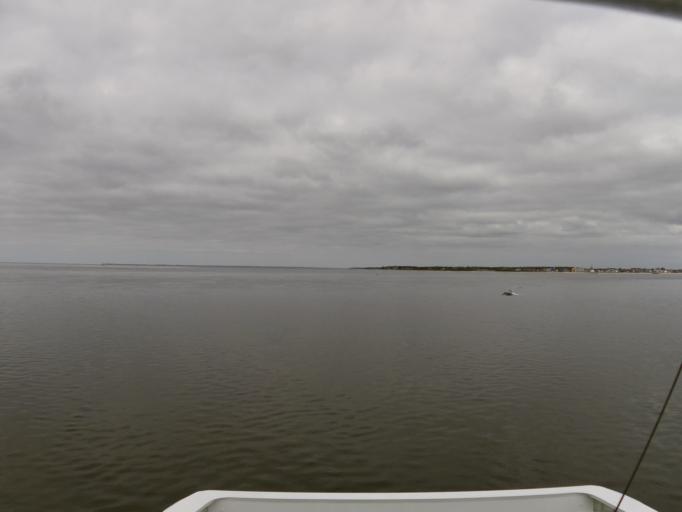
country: DE
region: Schleswig-Holstein
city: Langeness
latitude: 54.6758
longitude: 8.6000
